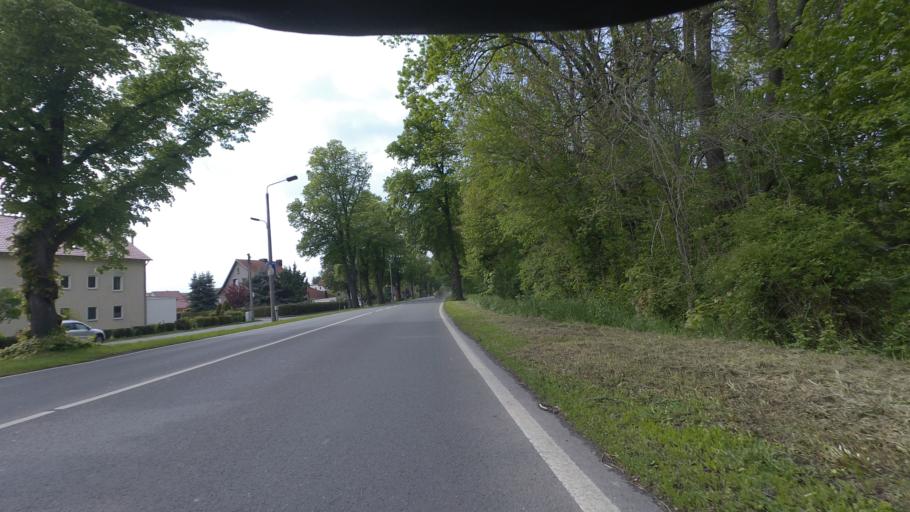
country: DE
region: Saxony-Anhalt
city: Halberstadt
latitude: 51.8975
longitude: 11.0333
